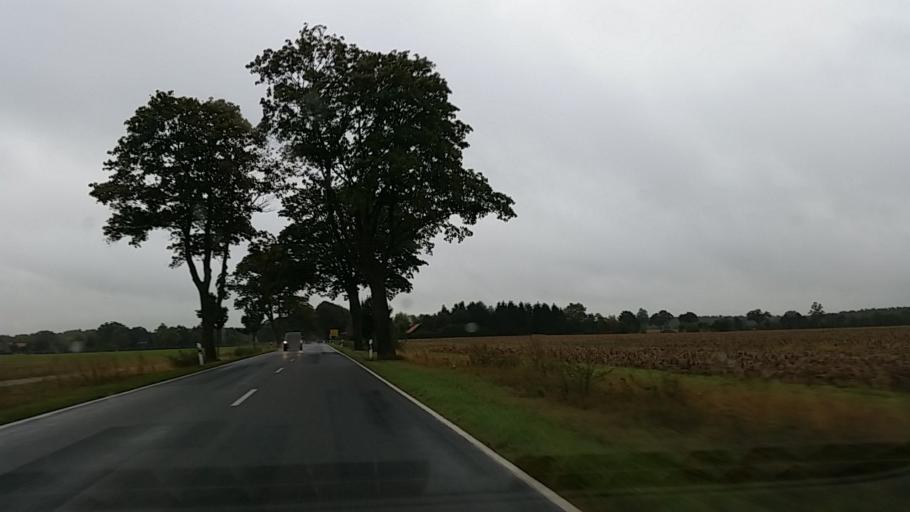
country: DE
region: Lower Saxony
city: Brome
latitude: 52.5771
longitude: 10.9322
